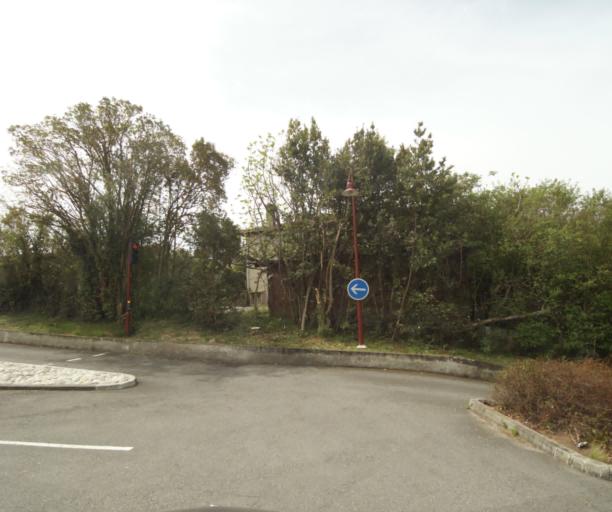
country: FR
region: Midi-Pyrenees
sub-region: Departement de la Haute-Garonne
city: Pechabou
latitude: 43.5006
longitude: 1.5075
